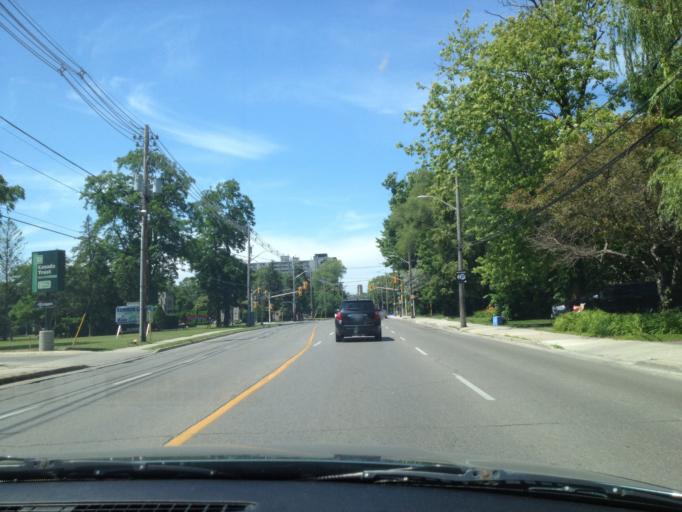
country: CA
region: Ontario
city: London
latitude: 43.0084
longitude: -81.2606
